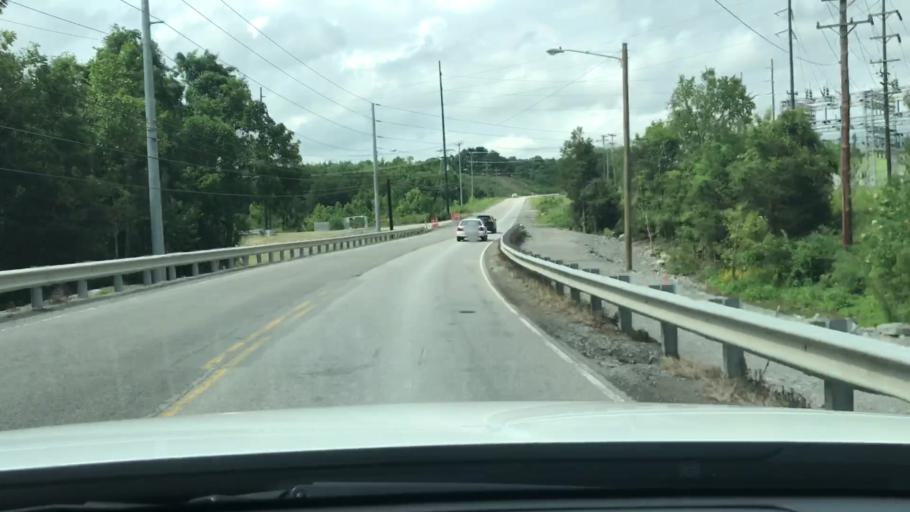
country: US
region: Tennessee
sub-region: Davidson County
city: Oak Hill
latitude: 36.0954
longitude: -86.6906
